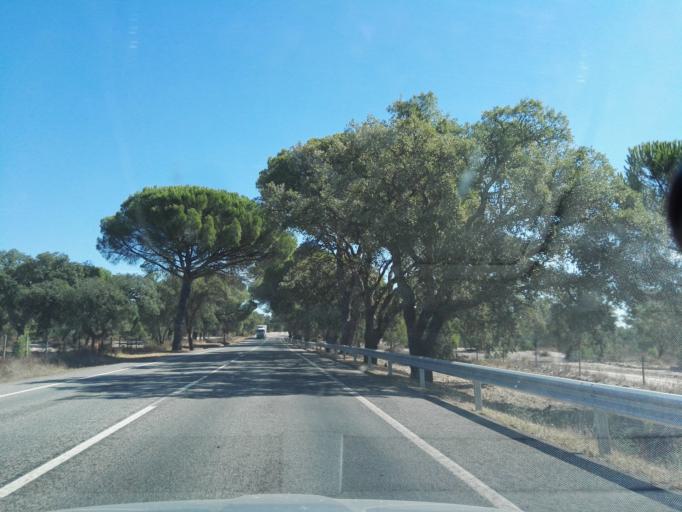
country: PT
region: Santarem
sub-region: Benavente
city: Poceirao
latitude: 38.8456
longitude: -8.7559
